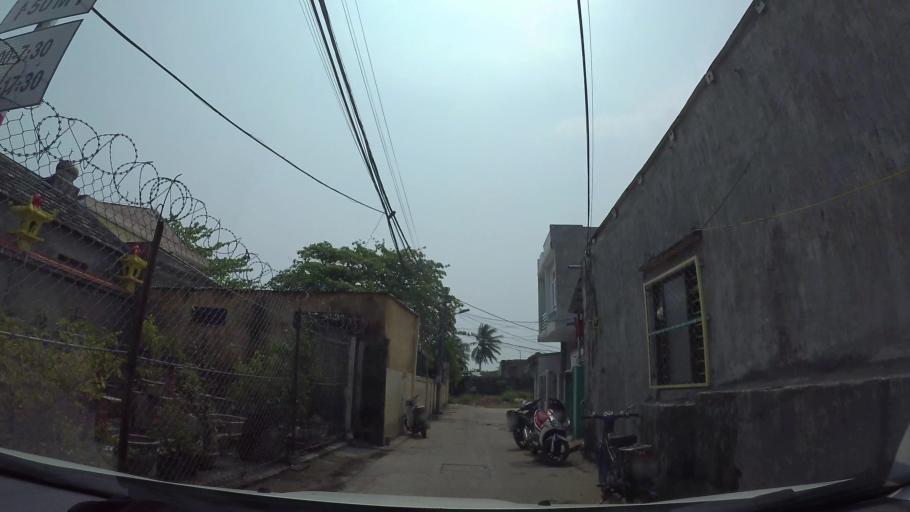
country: VN
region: Da Nang
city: Son Tra
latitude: 16.1010
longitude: 108.2549
